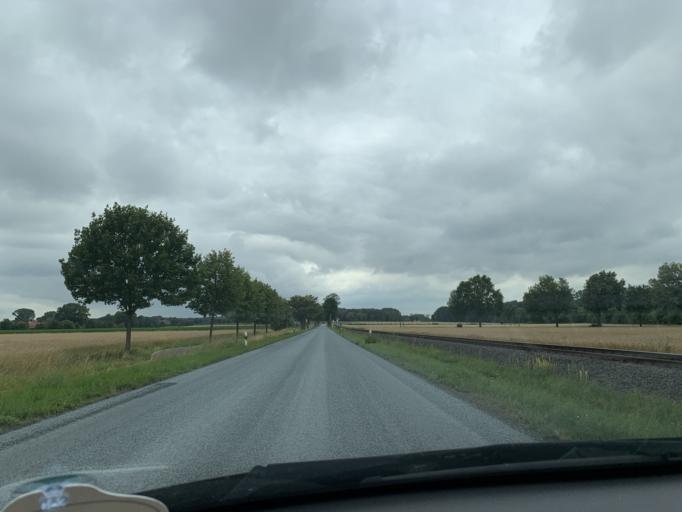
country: DE
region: North Rhine-Westphalia
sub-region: Regierungsbezirk Munster
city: Wadersloh
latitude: 51.6928
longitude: 8.2829
